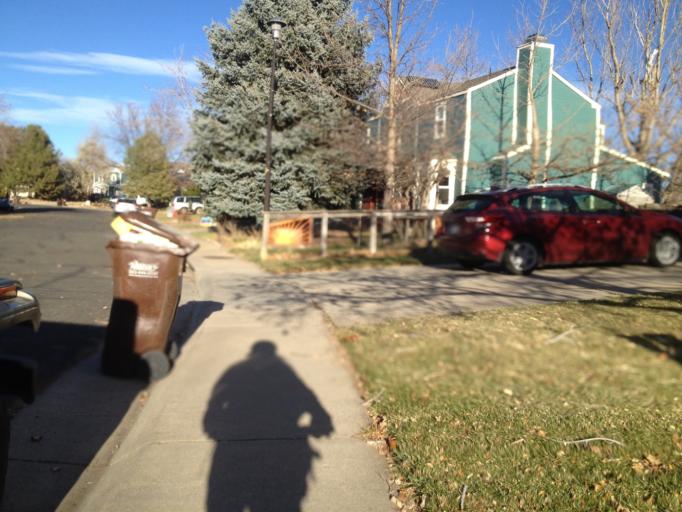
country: US
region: Colorado
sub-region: Boulder County
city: Louisville
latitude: 39.9730
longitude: -105.1480
